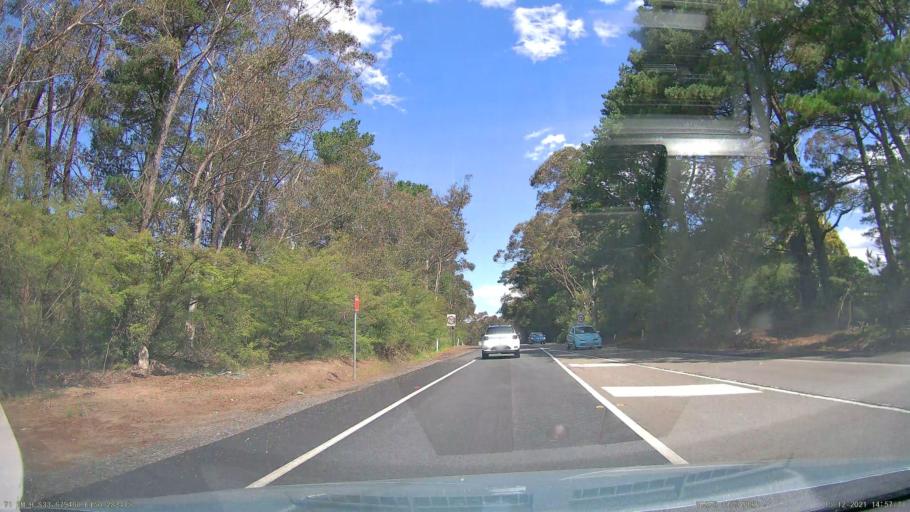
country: AU
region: New South Wales
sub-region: Blue Mountains Municipality
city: Blackheath
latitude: -33.6797
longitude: 150.2836
